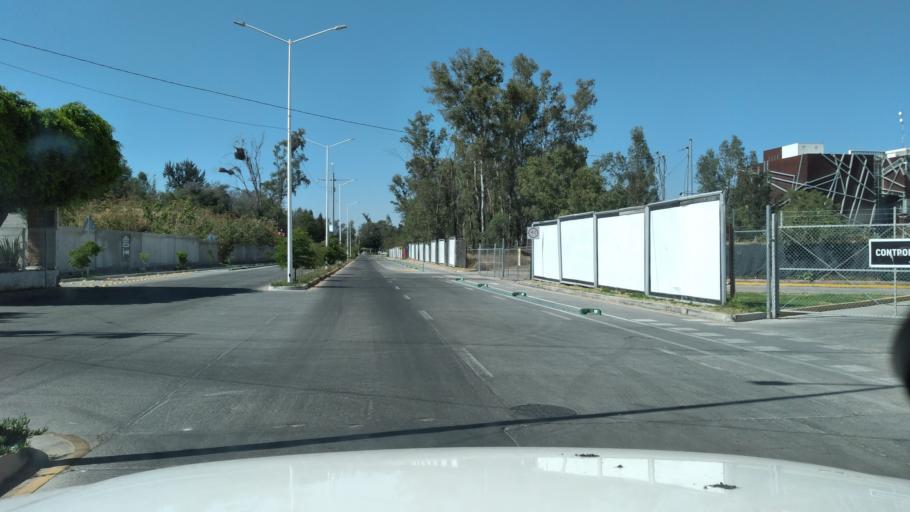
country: MX
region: Jalisco
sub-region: Zapopan
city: Zapopan
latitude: 20.7359
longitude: -103.3835
